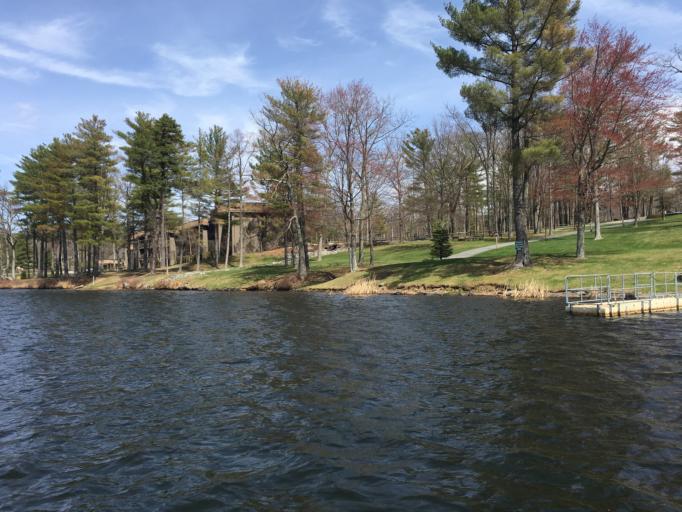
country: US
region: Pennsylvania
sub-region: Wayne County
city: Hawley
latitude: 41.5181
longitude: -75.0913
